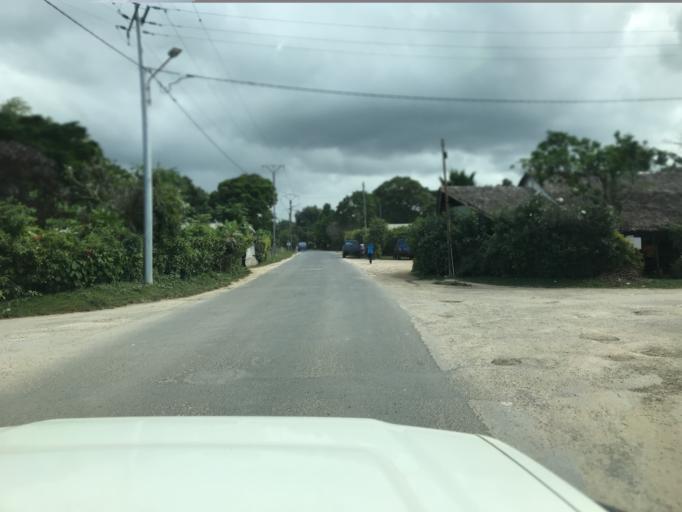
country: VU
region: Sanma
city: Luganville
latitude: -15.5121
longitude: 167.1743
